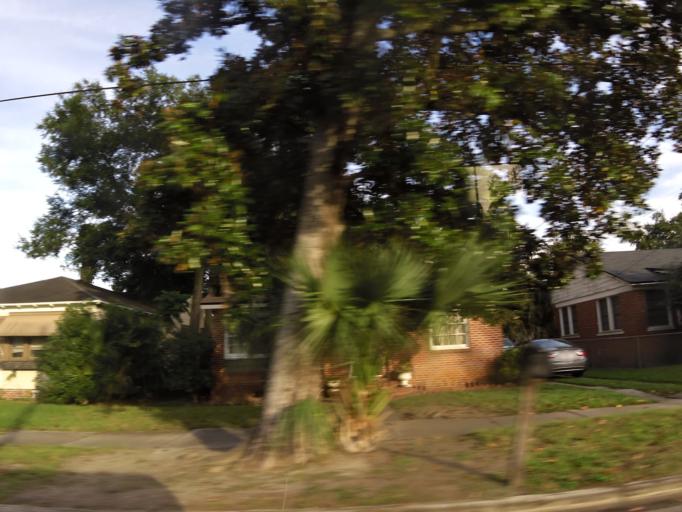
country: US
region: Florida
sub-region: Duval County
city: Jacksonville
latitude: 30.3764
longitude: -81.6566
